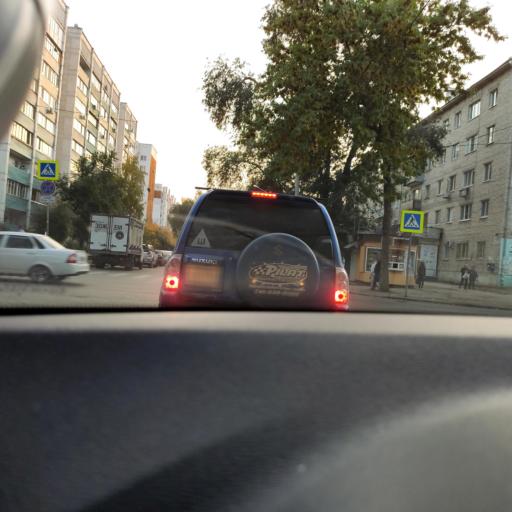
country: RU
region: Samara
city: Petra-Dubrava
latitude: 53.2290
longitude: 50.2746
